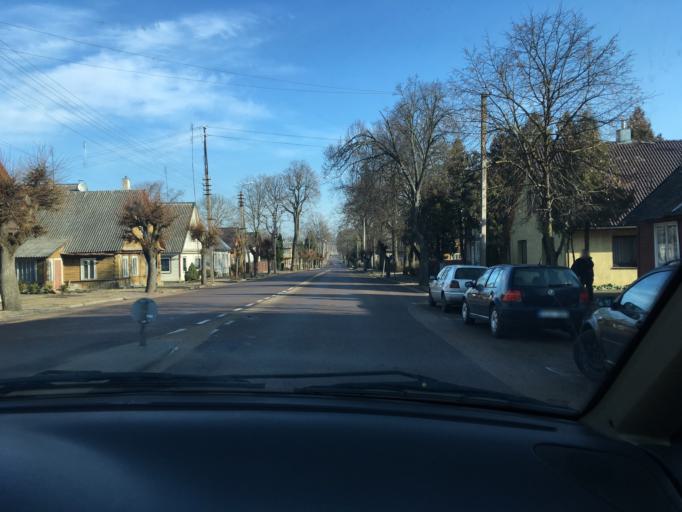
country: LT
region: Panevezys
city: Rokiskis
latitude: 55.7472
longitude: 25.8408
